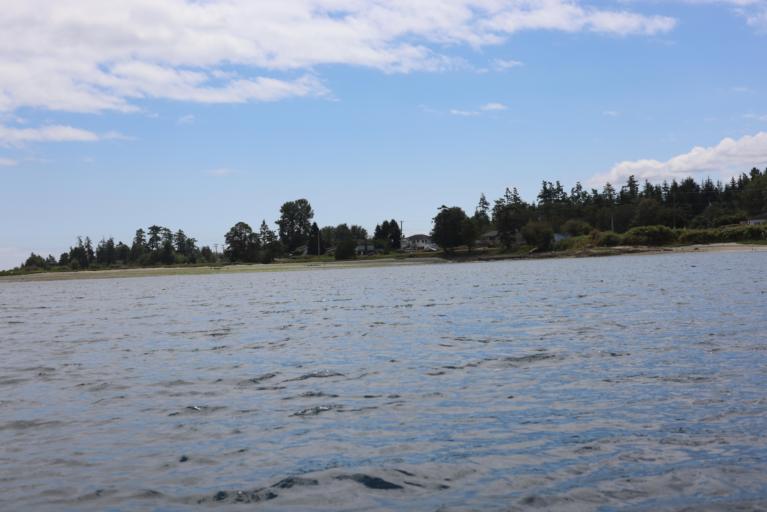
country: CA
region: British Columbia
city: North Saanich
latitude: 48.5940
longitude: -123.3797
